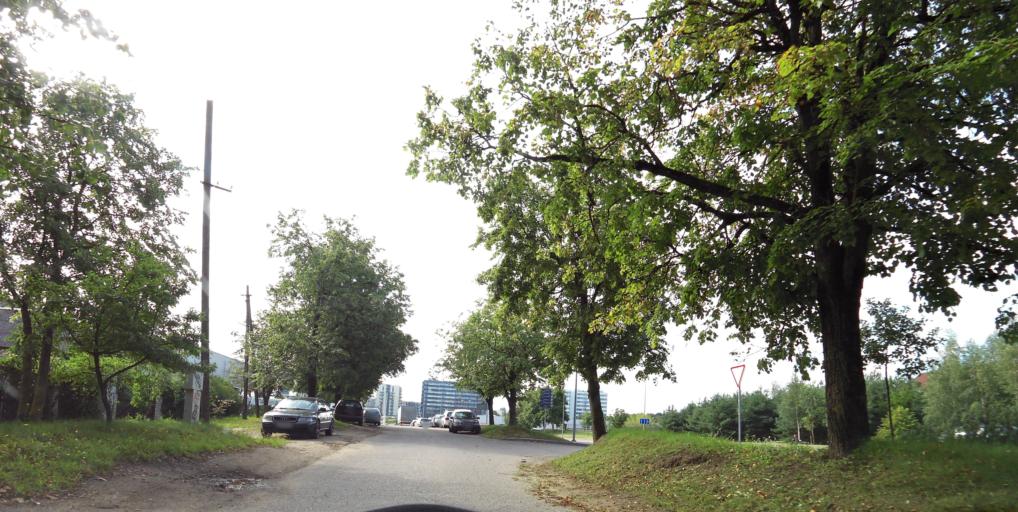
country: LT
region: Vilnius County
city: Seskine
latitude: 54.7254
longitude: 25.2810
